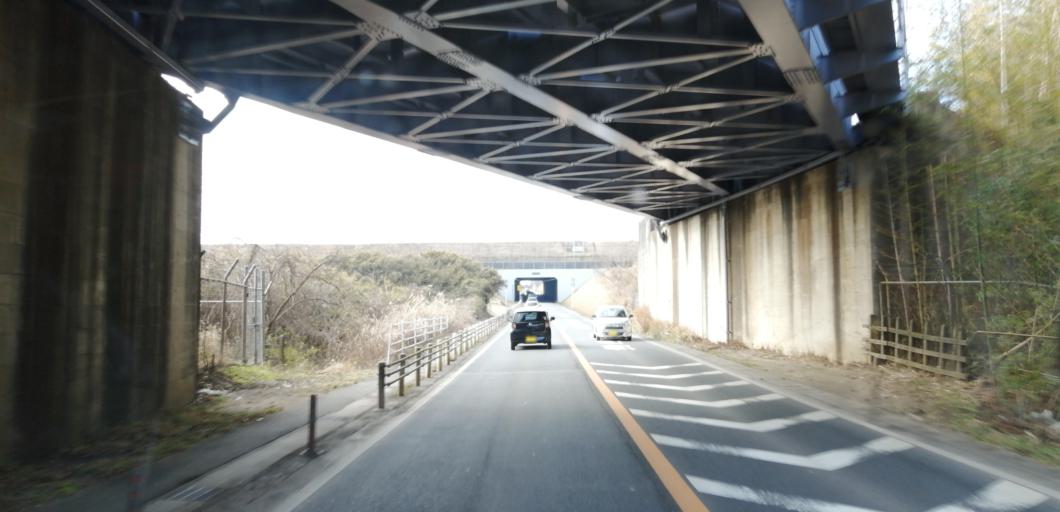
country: JP
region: Chiba
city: Narita
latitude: 35.7781
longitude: 140.3686
